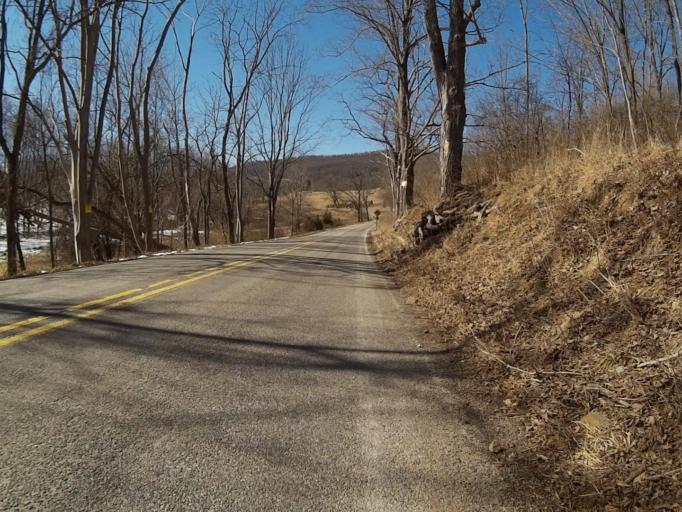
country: US
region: Pennsylvania
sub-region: Centre County
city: Park Forest Village
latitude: 40.8345
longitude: -77.9361
